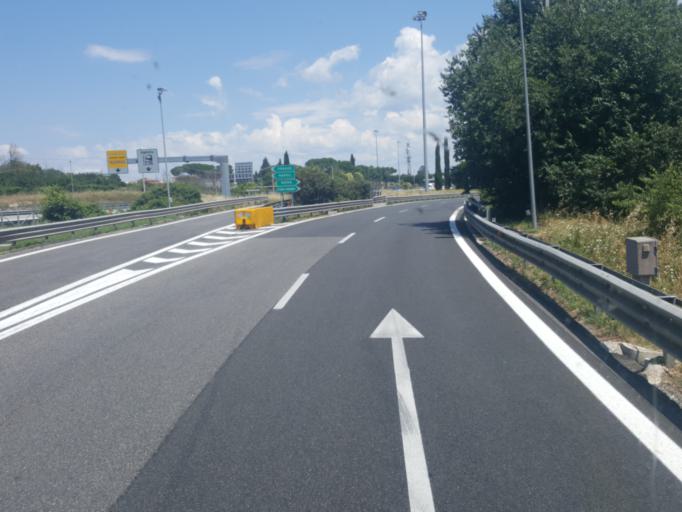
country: IT
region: Latium
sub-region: Citta metropolitana di Roma Capitale
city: Bivio di Capanelle
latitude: 42.1368
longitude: 12.6046
